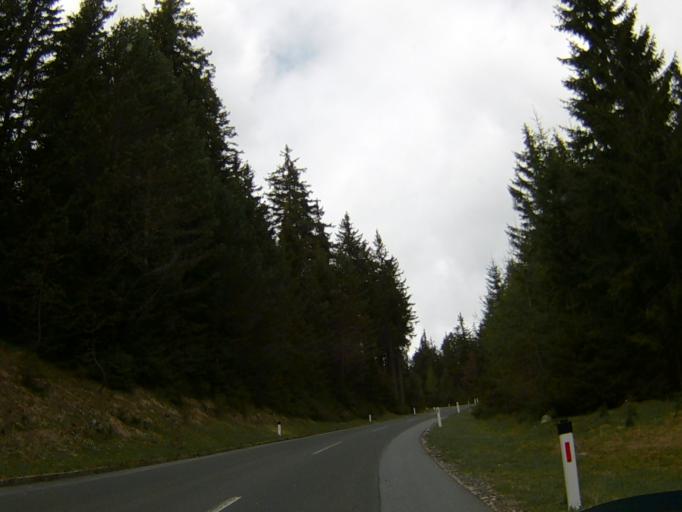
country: AT
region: Carinthia
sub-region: Politischer Bezirk Villach Land
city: Arnoldstein
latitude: 46.5920
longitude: 13.7512
